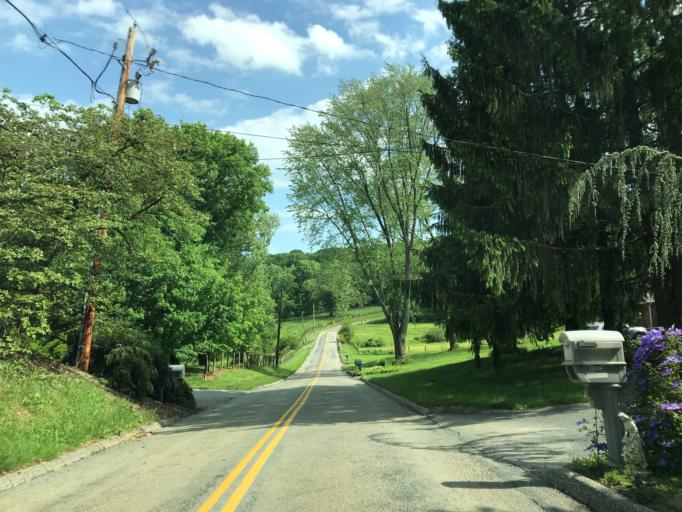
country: US
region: Maryland
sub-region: Harford County
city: Bel Air North
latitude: 39.6553
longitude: -76.3774
